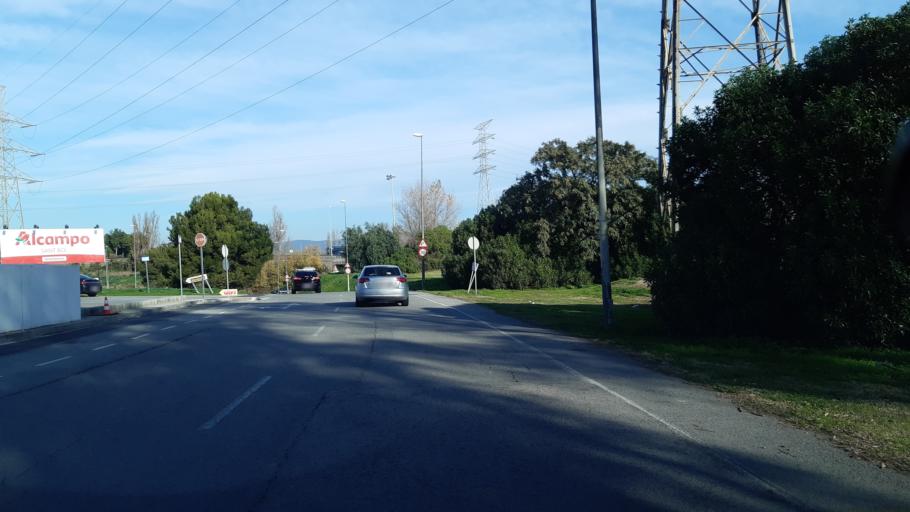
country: ES
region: Catalonia
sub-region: Provincia de Barcelona
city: Sant Boi de Llobregat
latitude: 41.3313
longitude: 2.0548
